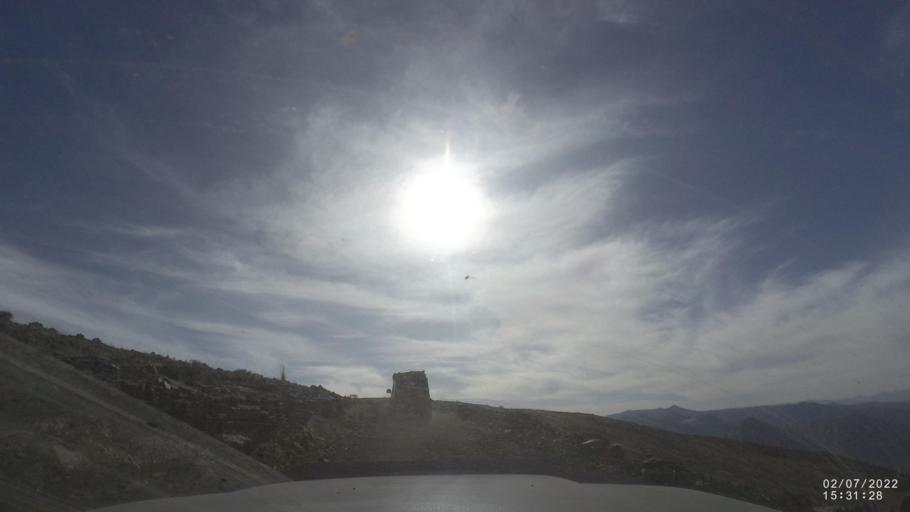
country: BO
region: Cochabamba
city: Irpa Irpa
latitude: -17.8831
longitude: -66.4139
